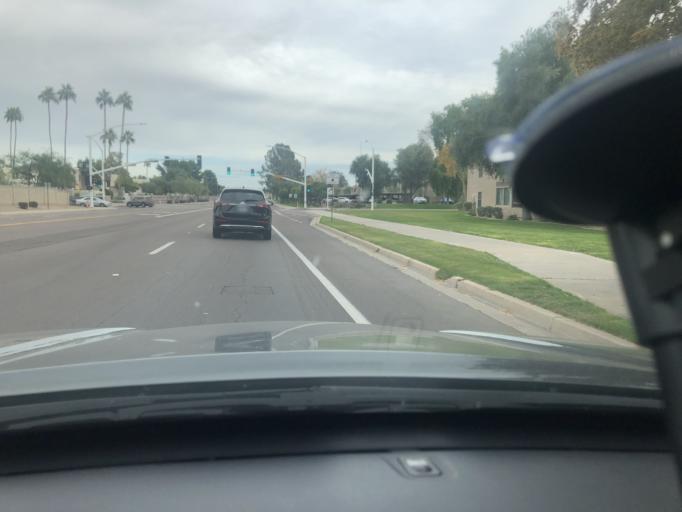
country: US
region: Arizona
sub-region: Maricopa County
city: Scottsdale
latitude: 33.5239
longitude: -111.9137
